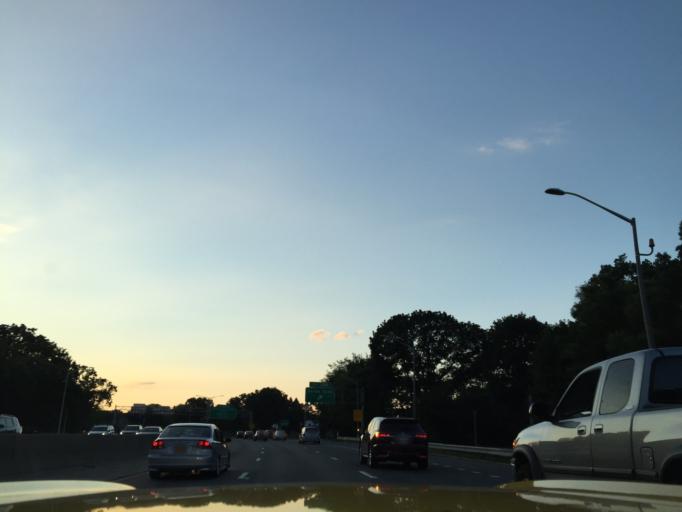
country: US
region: New York
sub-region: Nassau County
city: Bellerose
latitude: 40.7381
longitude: -73.7238
